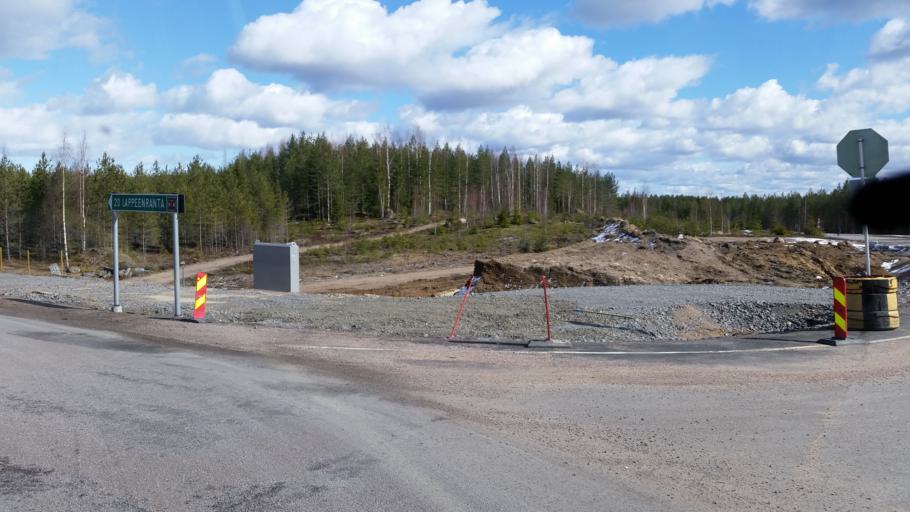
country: FI
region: South Karelia
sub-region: Lappeenranta
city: Lemi
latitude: 60.9755
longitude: 27.8728
